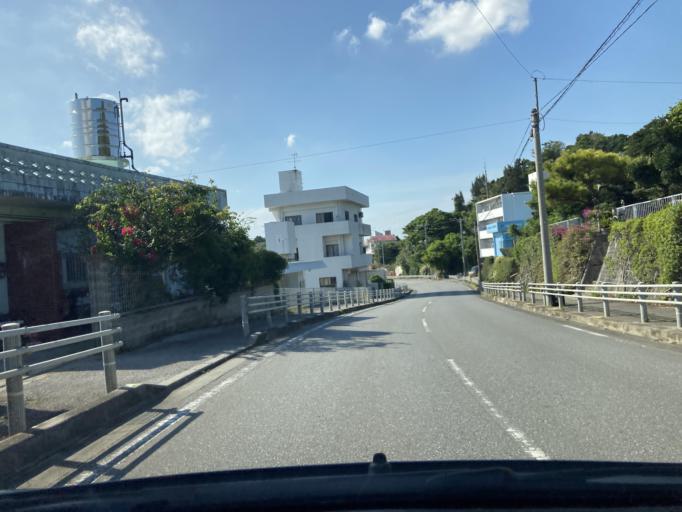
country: JP
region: Okinawa
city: Chatan
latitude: 26.2965
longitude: 127.7892
